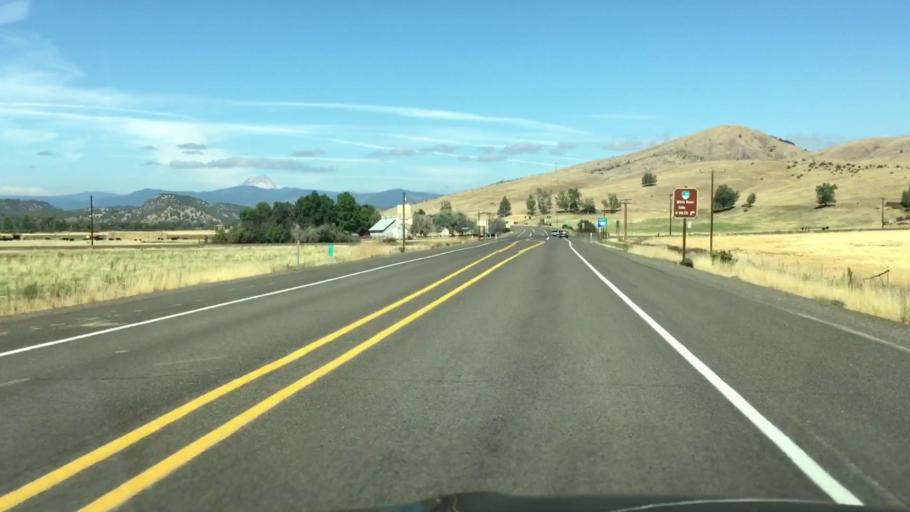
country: US
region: Oregon
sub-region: Wasco County
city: The Dalles
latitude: 45.2511
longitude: -121.1721
